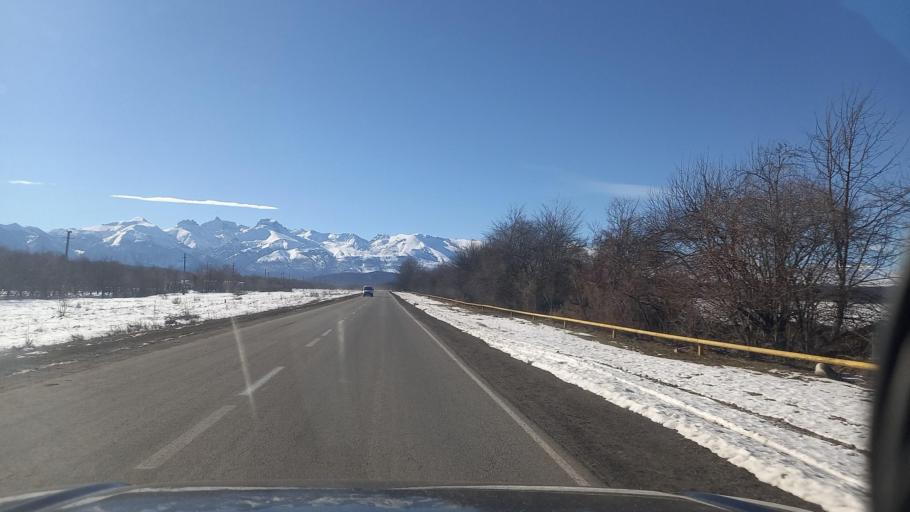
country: RU
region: North Ossetia
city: Chikola
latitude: 43.1730
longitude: 43.8720
